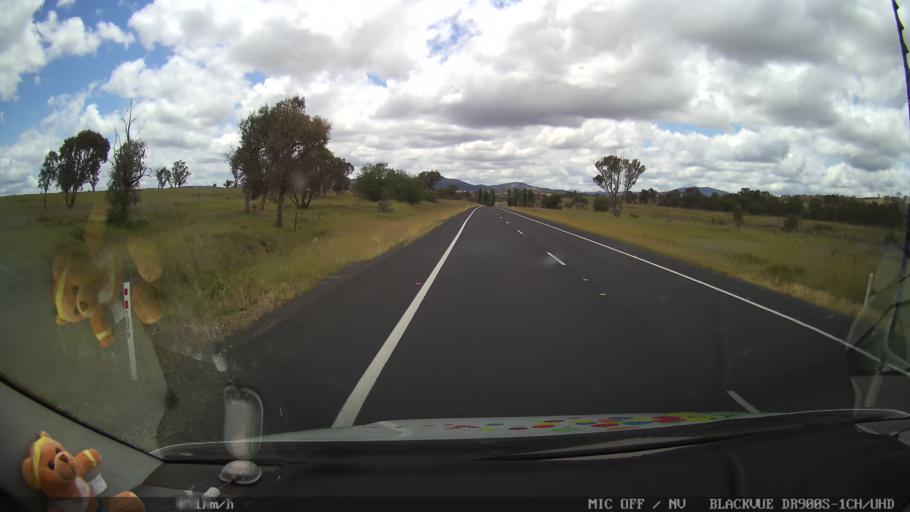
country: AU
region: New South Wales
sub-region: Glen Innes Severn
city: Glen Innes
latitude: -29.3923
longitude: 151.8823
